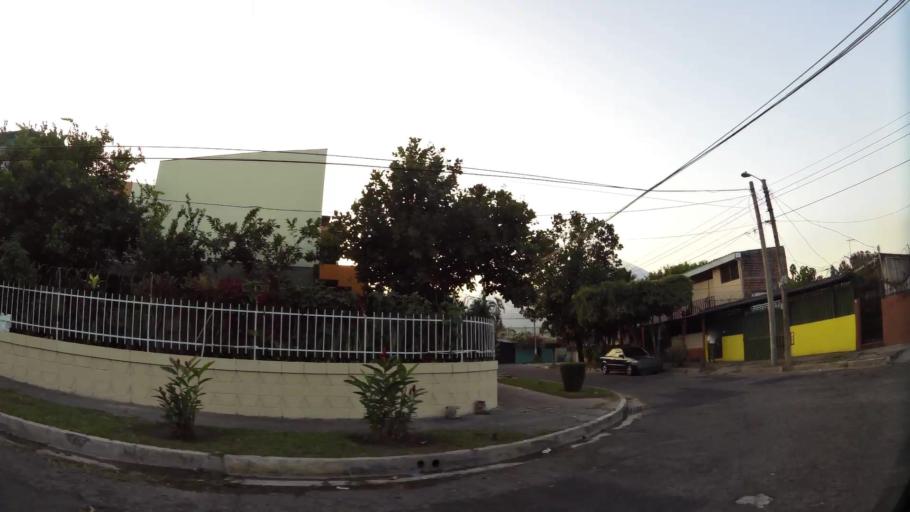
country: SV
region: San Salvador
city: Mejicanos
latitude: 13.7155
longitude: -89.2090
